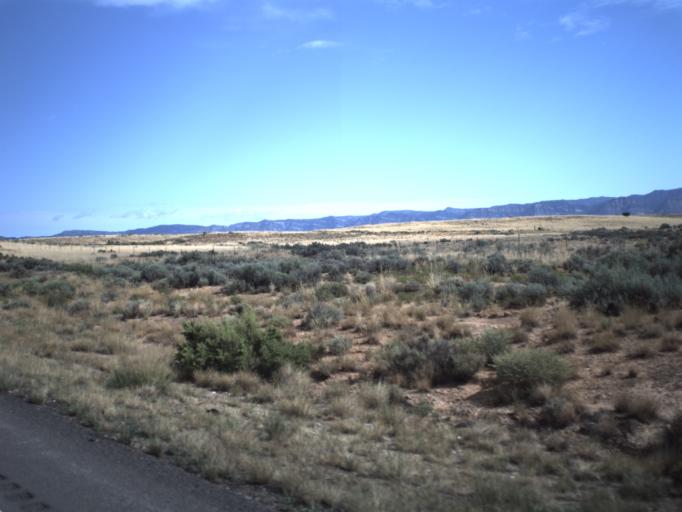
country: US
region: Utah
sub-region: Carbon County
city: East Carbon City
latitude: 39.5006
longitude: -110.5274
